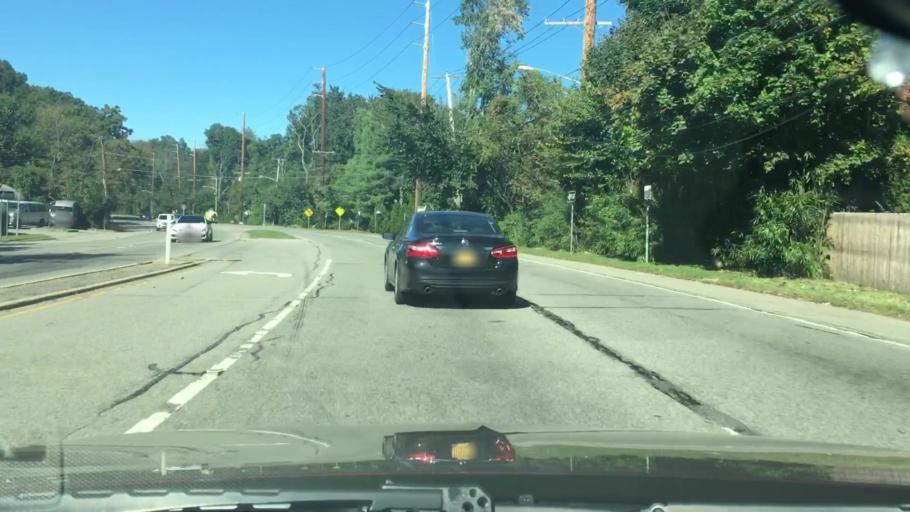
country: US
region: New York
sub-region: Nassau County
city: Flower Hill
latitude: 40.8061
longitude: -73.6690
